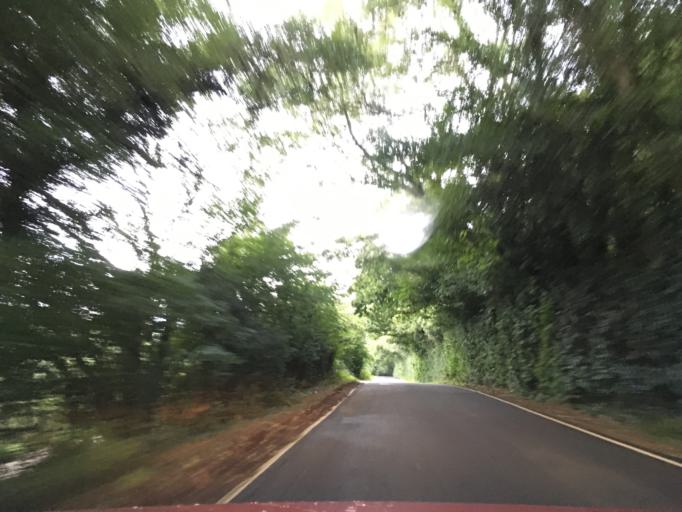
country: GB
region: Wales
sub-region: Monmouthshire
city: Llangwm
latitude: 51.6558
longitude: -2.8550
